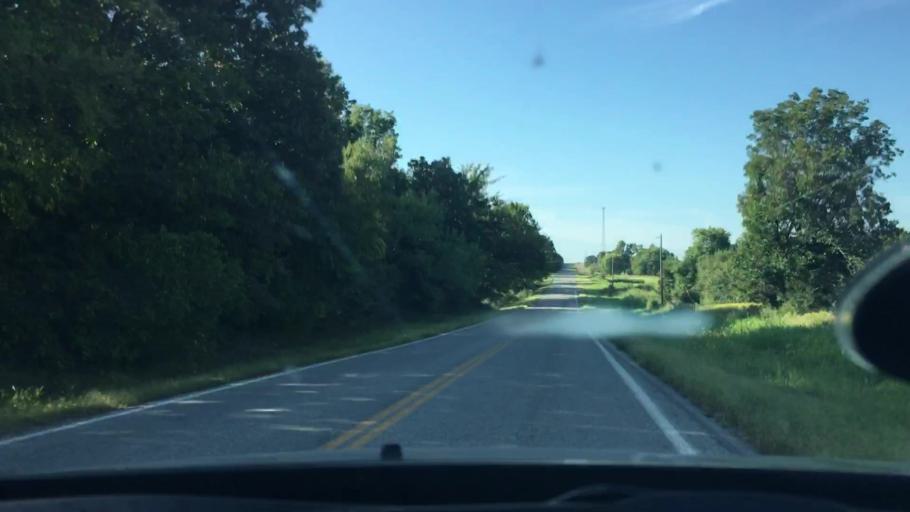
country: US
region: Oklahoma
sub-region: Coal County
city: Coalgate
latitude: 34.6244
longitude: -96.4243
